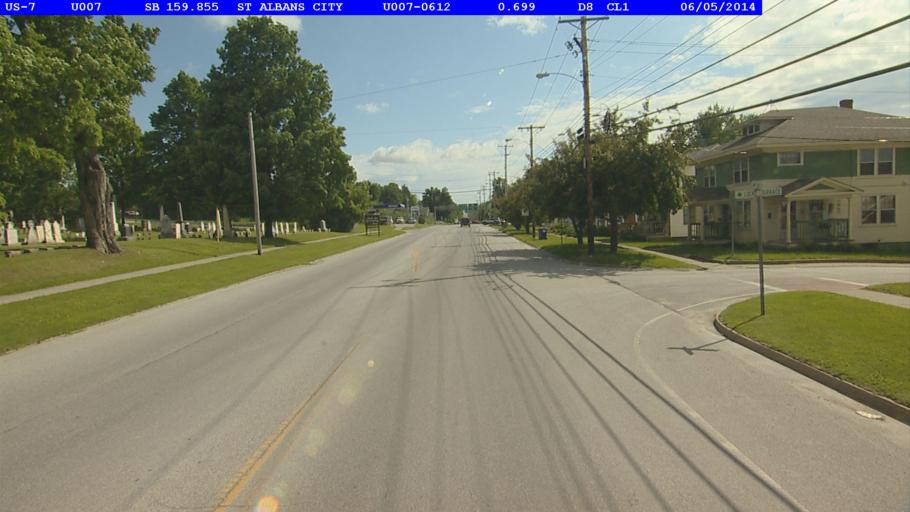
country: US
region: Vermont
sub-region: Franklin County
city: Saint Albans
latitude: 44.8035
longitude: -73.0873
